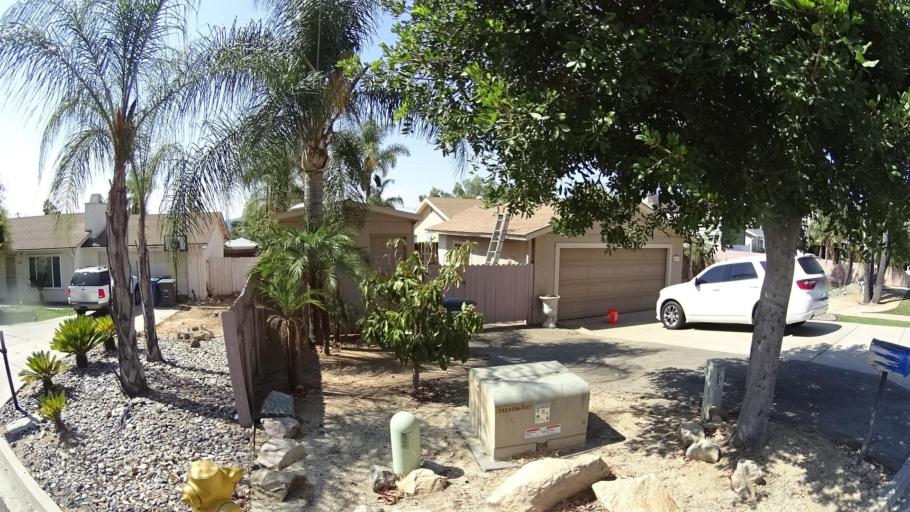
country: US
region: California
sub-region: San Diego County
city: Winter Gardens
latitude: 32.8271
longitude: -116.9231
